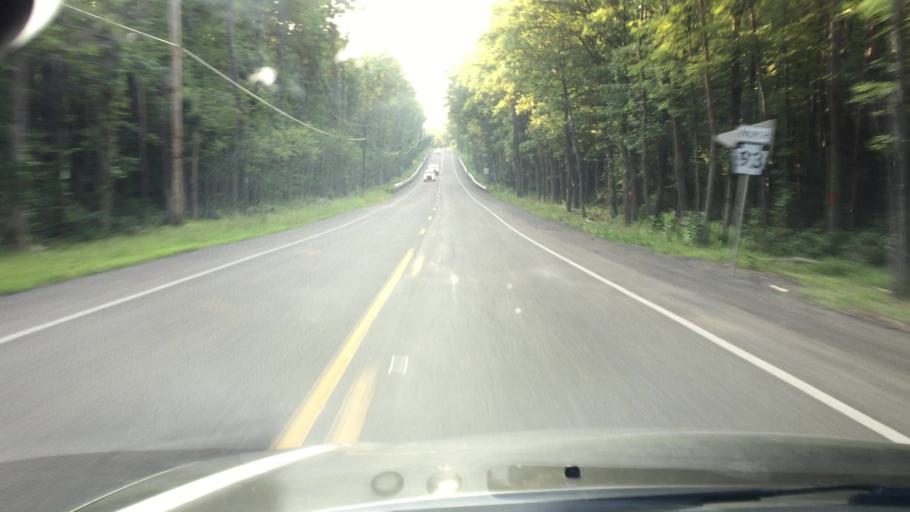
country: US
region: Pennsylvania
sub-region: Carbon County
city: Weatherly
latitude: 40.9065
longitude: -75.8256
